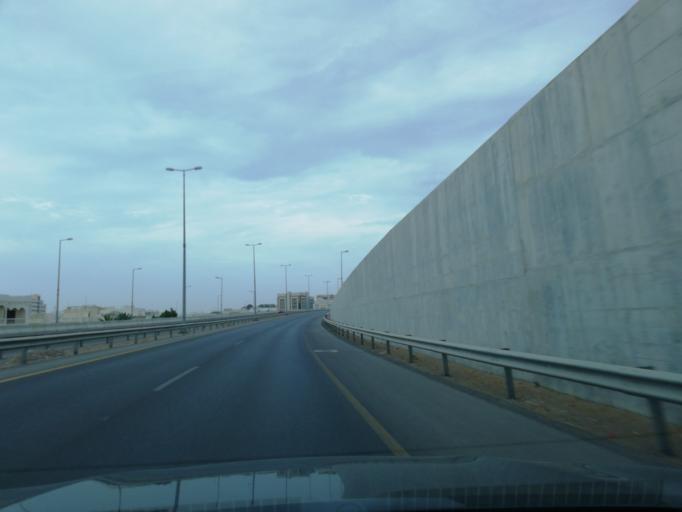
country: OM
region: Muhafazat Masqat
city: Bawshar
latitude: 23.5903
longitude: 58.4412
